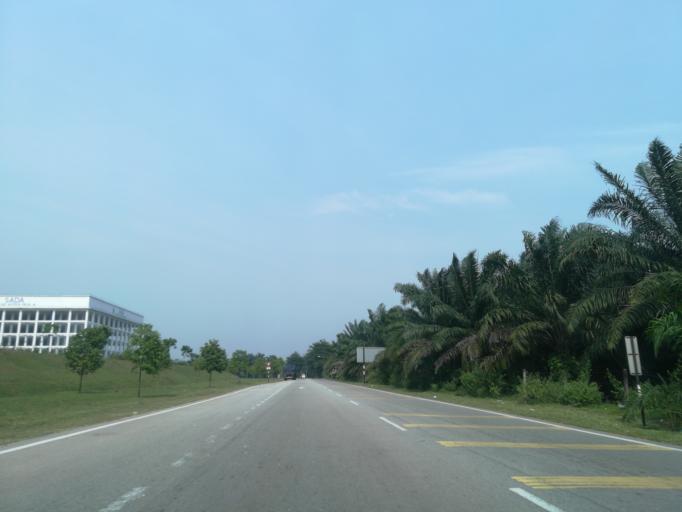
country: MY
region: Penang
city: Tasek Glugor
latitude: 5.4530
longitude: 100.5561
